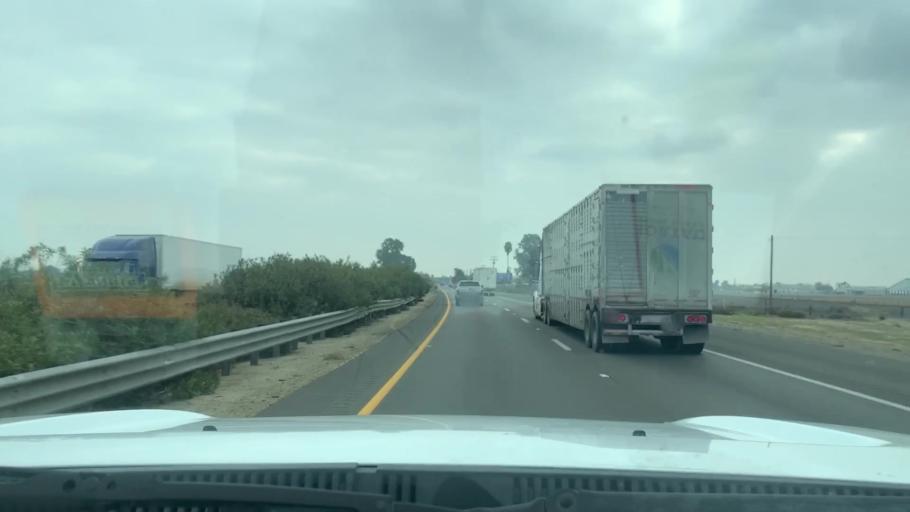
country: US
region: California
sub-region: Tulare County
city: Tipton
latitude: 36.0723
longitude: -119.3172
